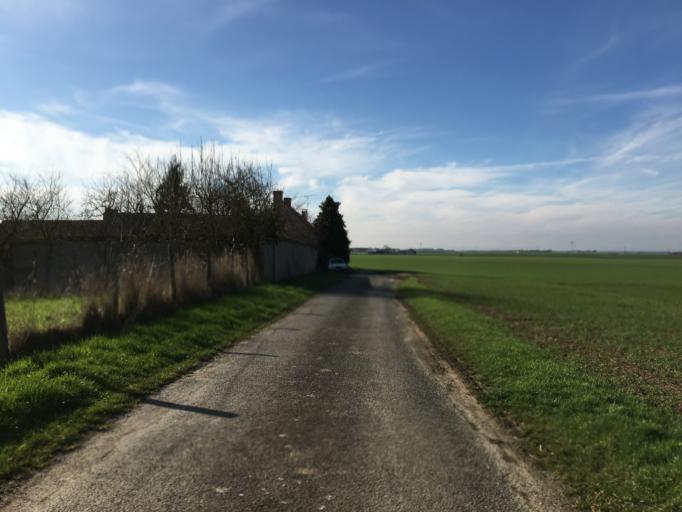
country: FR
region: Centre
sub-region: Departement du Loiret
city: Tavers
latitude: 47.7586
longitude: 1.5887
